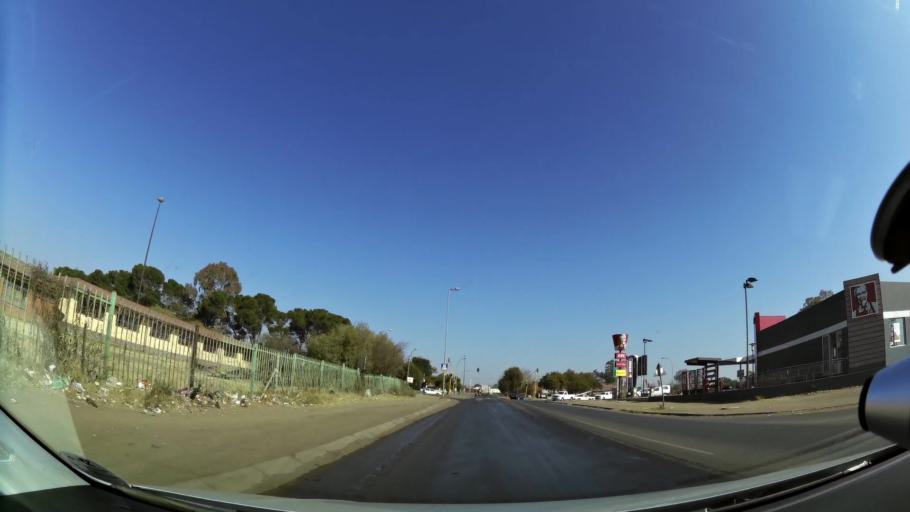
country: ZA
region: Orange Free State
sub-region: Mangaung Metropolitan Municipality
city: Bloemfontein
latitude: -29.1349
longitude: 26.2272
